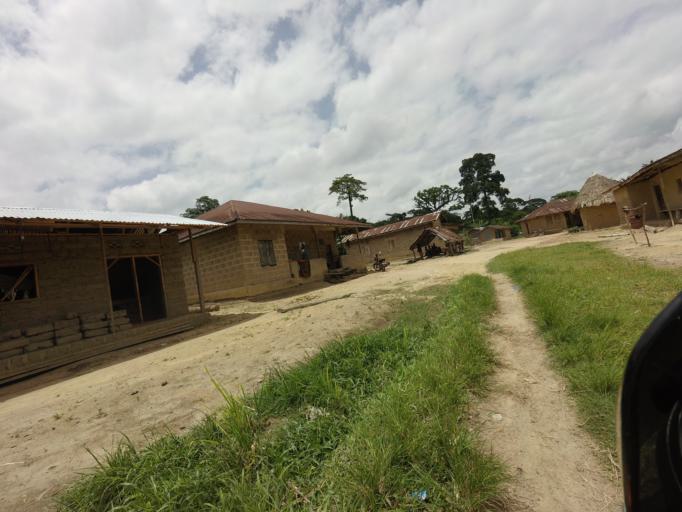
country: SL
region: Eastern Province
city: Tombodu
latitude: 8.1819
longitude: -10.5876
